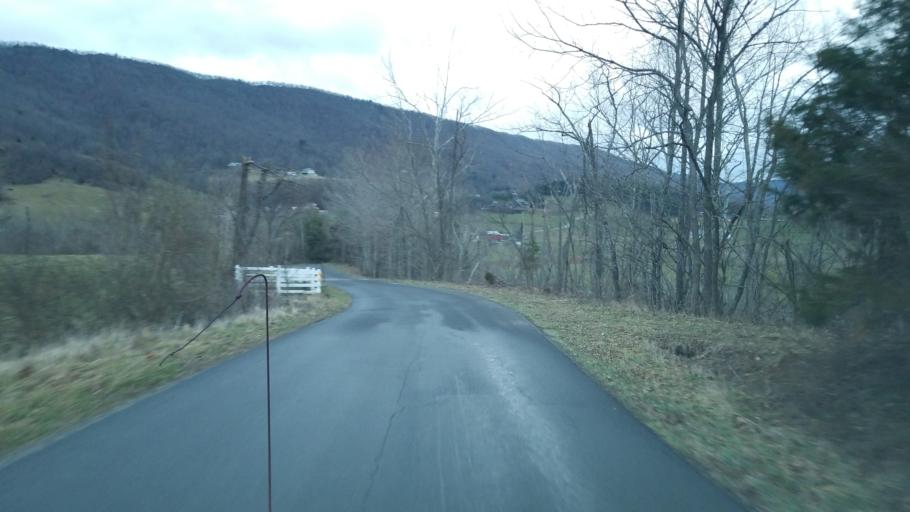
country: US
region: Virginia
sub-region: Pulaski County
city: Pulaski
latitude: 37.1634
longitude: -80.8582
